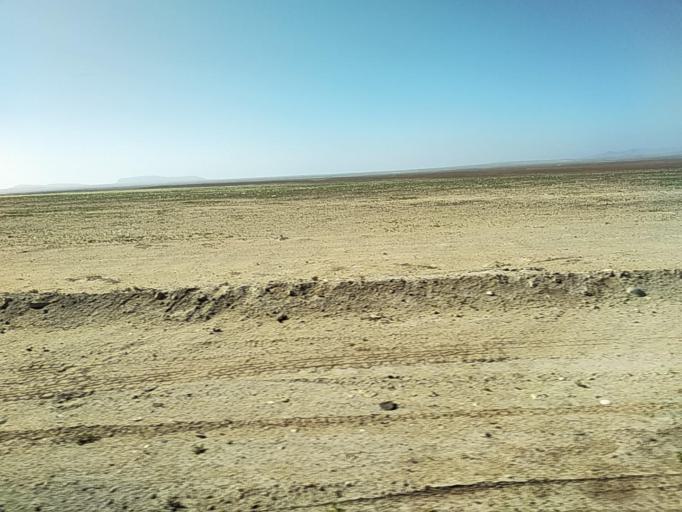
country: CL
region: Atacama
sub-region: Provincia de Copiapo
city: Copiapo
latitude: -27.3166
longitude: -70.8668
